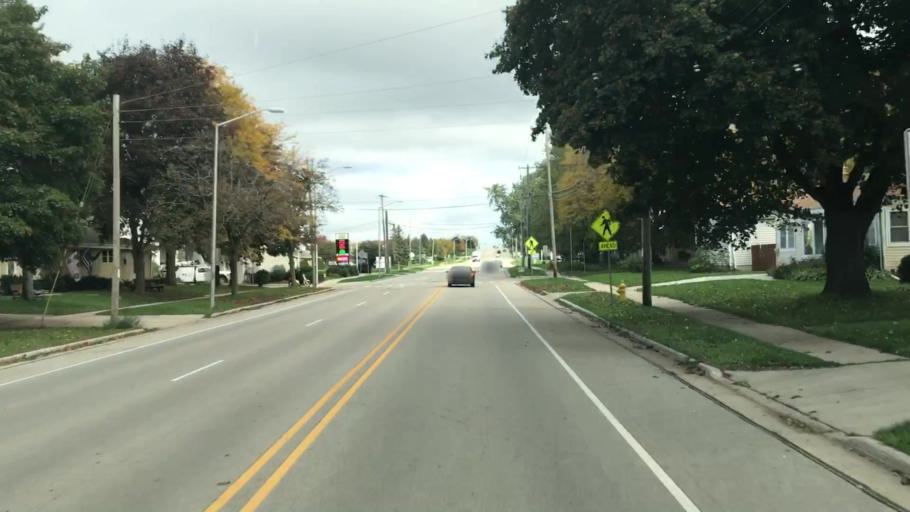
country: US
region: Wisconsin
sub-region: Waukesha County
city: Waukesha
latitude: 43.0253
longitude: -88.2260
